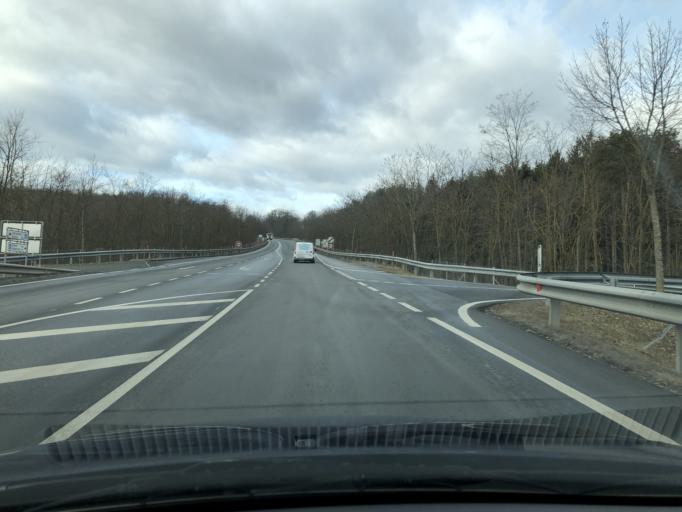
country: AT
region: Burgenland
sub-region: Politischer Bezirk Oberwart
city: Hannersdorf
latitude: 47.2606
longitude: 16.3676
